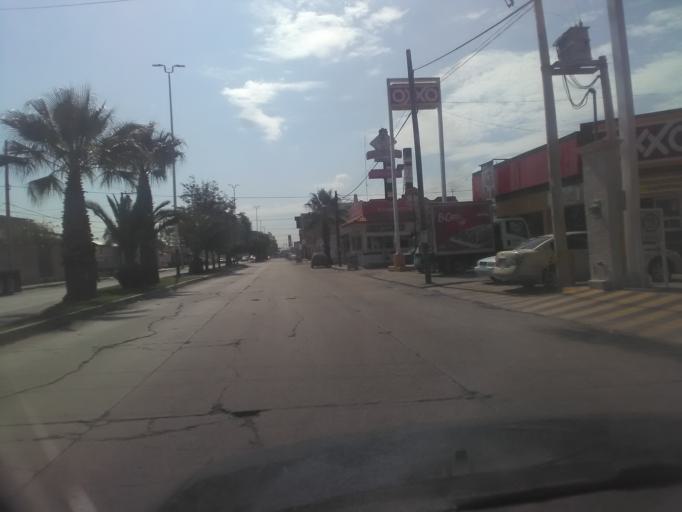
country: MX
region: Durango
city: Victoria de Durango
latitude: 24.0200
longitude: -104.6359
